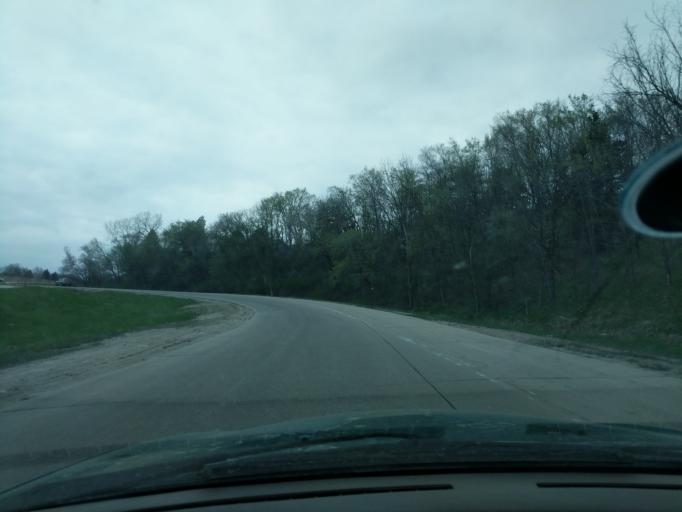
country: US
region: Nebraska
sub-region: Douglas County
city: Ralston
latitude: 41.2346
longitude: -96.0838
